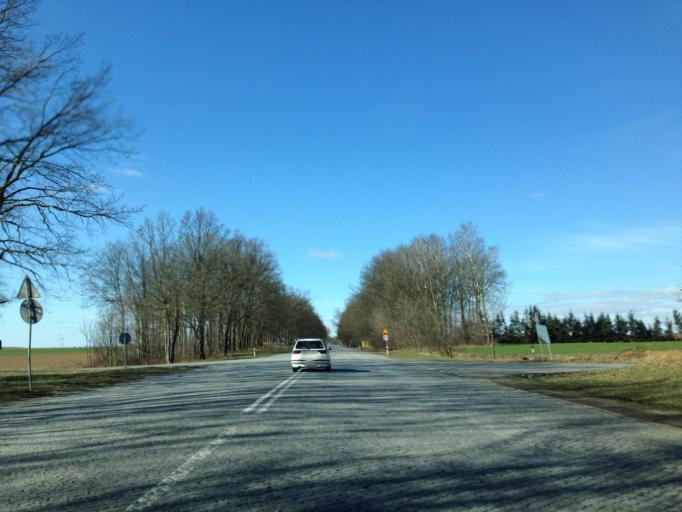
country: PL
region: Pomeranian Voivodeship
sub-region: Powiat tczewski
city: Tczew
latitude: 54.0496
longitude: 18.7902
